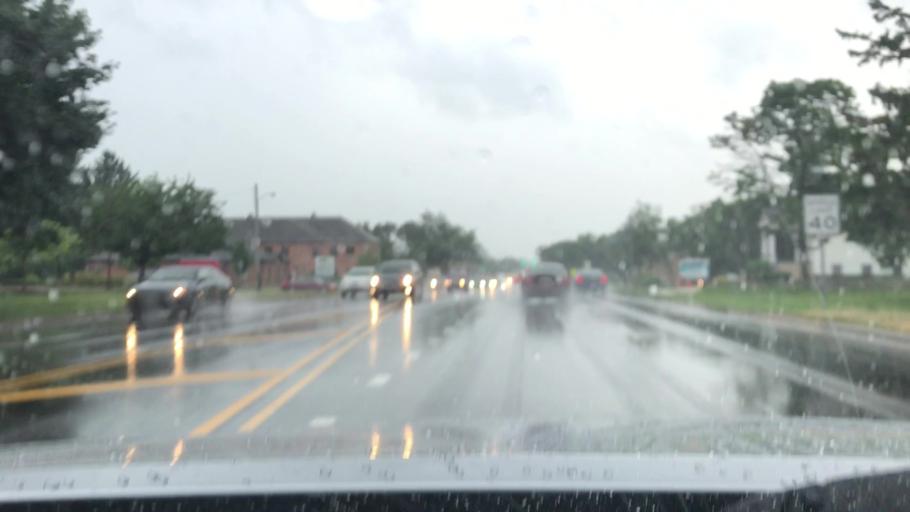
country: US
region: Illinois
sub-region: DuPage County
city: Lisle
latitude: 41.8017
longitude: -88.0716
